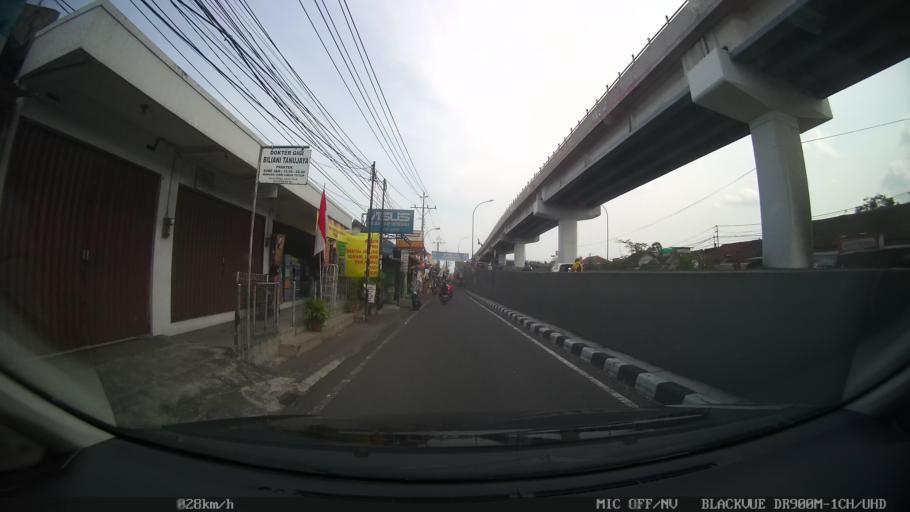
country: ID
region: Daerah Istimewa Yogyakarta
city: Depok
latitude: -7.7842
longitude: 110.4106
